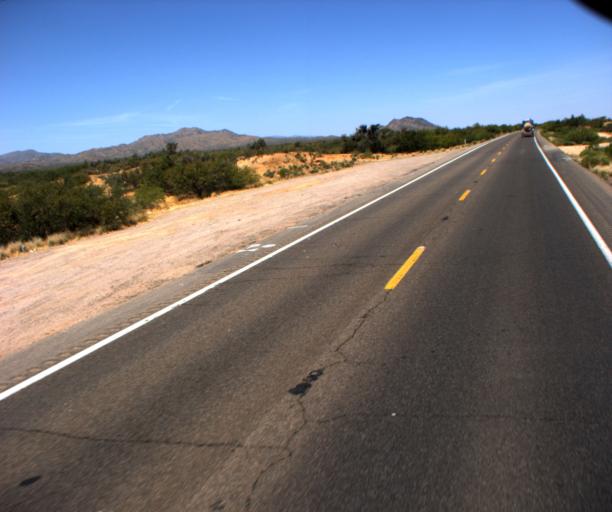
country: US
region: Arizona
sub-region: Gila County
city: Peridot
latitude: 33.3097
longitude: -110.5018
